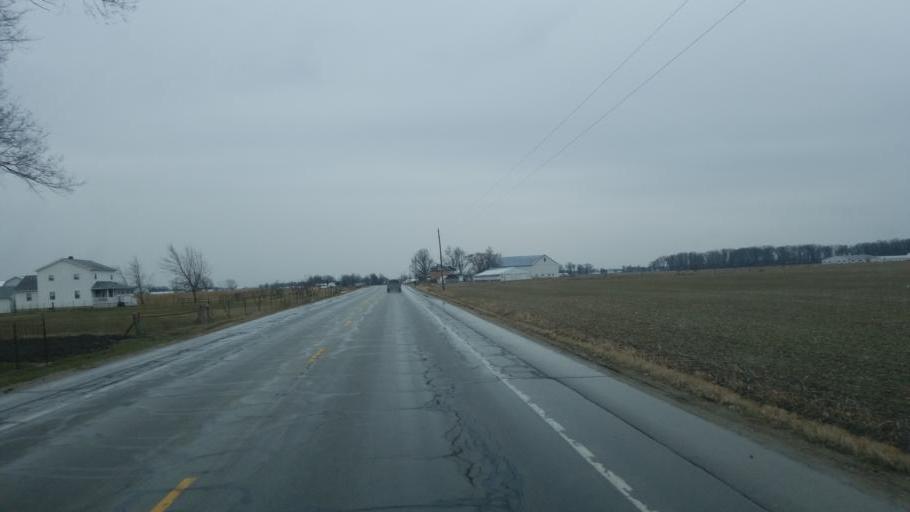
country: US
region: Indiana
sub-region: Adams County
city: Berne
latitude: 40.7212
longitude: -84.9559
